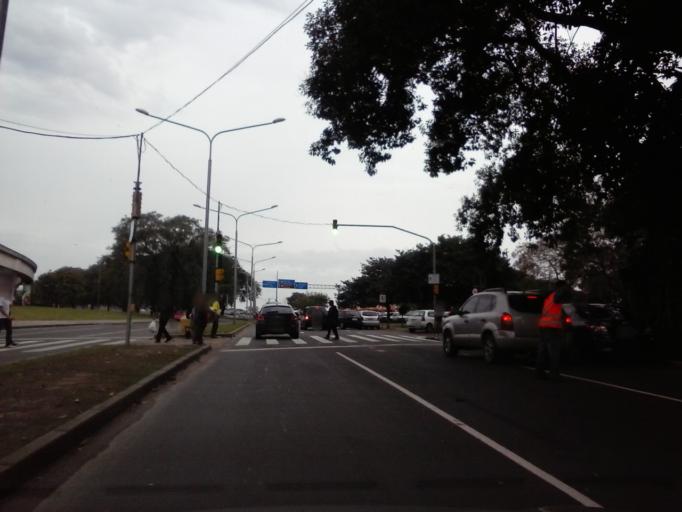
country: BR
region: Rio Grande do Sul
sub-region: Porto Alegre
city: Porto Alegre
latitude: -30.0343
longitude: -51.2405
